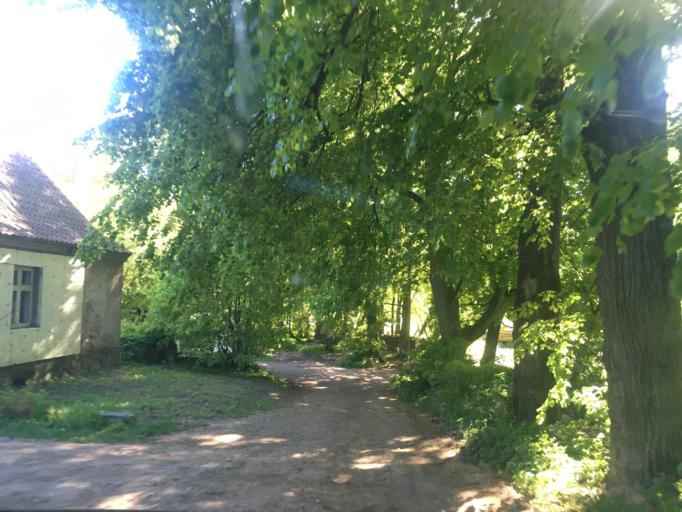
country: PL
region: Warmian-Masurian Voivodeship
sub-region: Powiat piski
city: Ruciane-Nida
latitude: 53.6552
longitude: 21.4826
